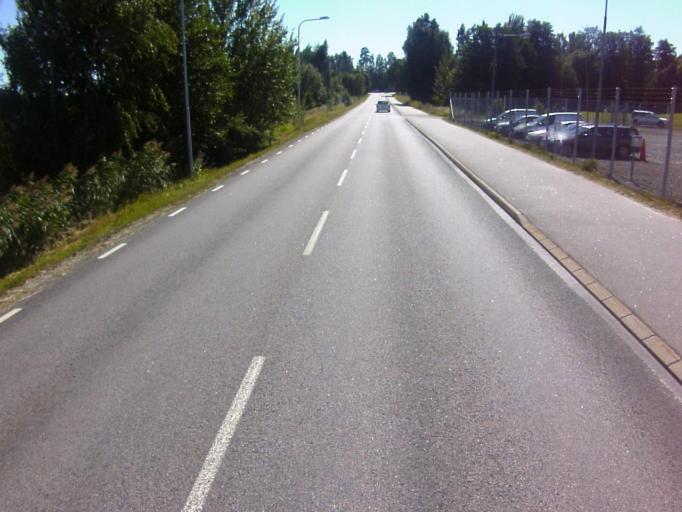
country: SE
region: Soedermanland
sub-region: Eskilstuna Kommun
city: Hallbybrunn
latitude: 59.3827
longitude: 16.4350
